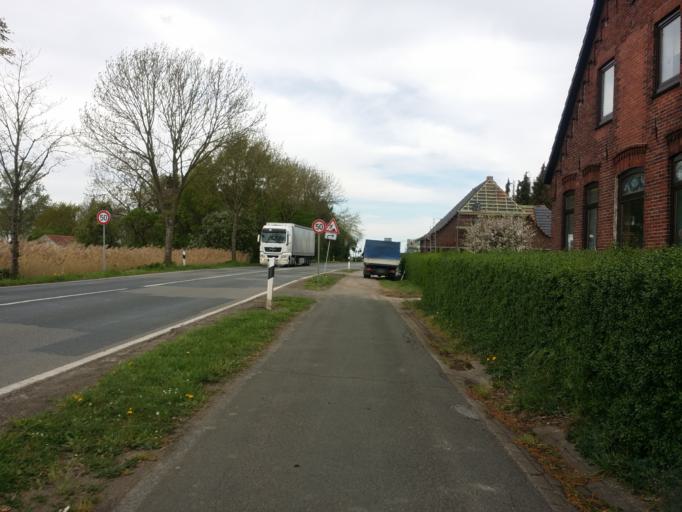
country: DE
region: Lower Saxony
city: Lemwerder
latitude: 53.1462
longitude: 8.5504
